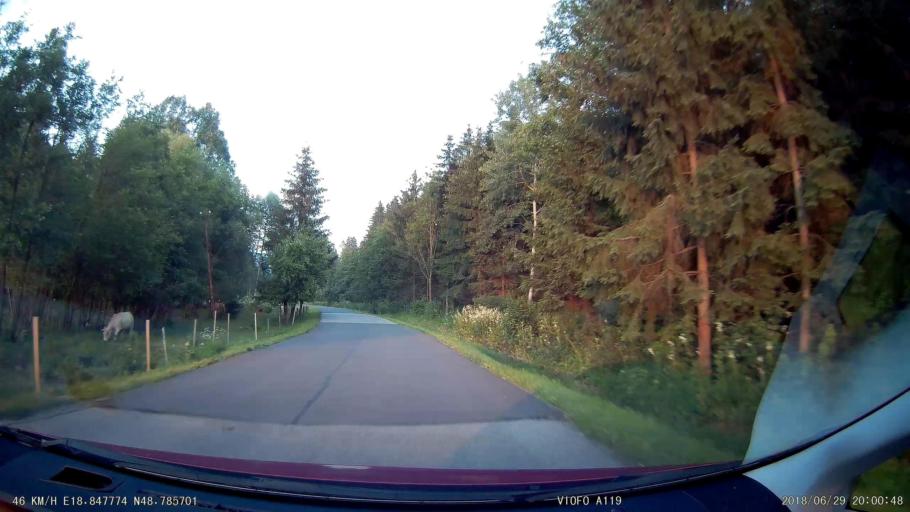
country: SK
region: Nitriansky
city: Handlova
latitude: 48.7856
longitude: 18.8480
